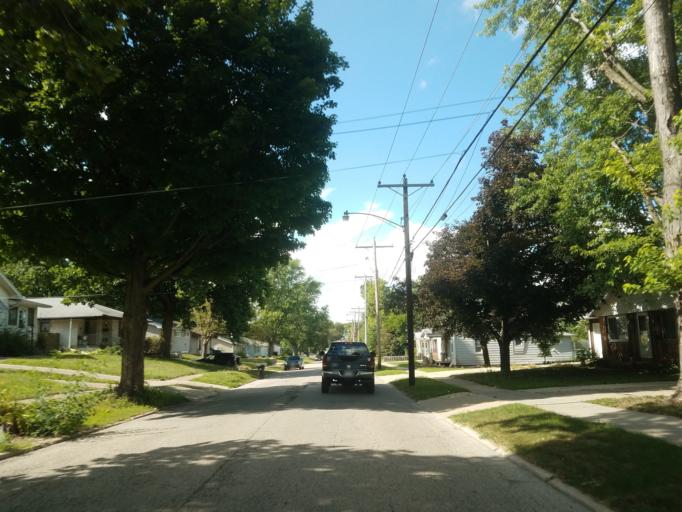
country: US
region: Illinois
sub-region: McLean County
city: Bloomington
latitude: 40.4912
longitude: -88.9819
